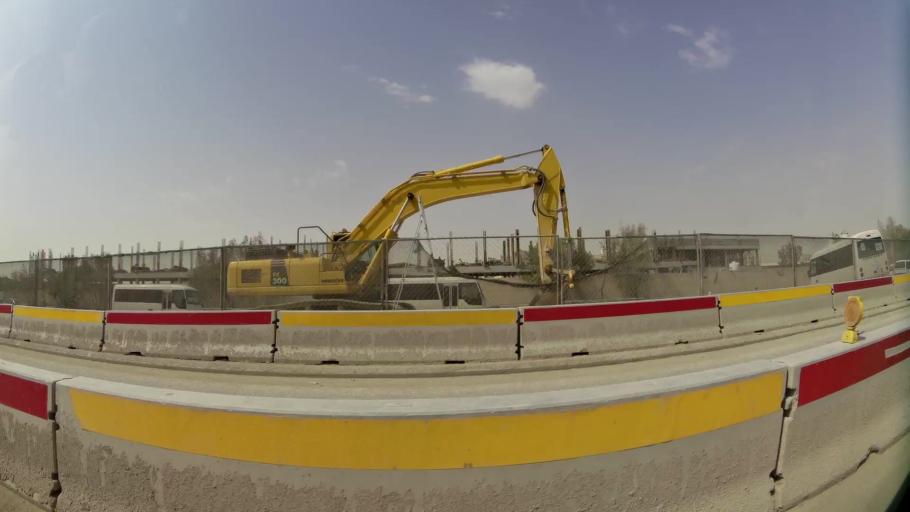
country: QA
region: Al Wakrah
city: Al Wukayr
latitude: 25.1670
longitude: 51.4522
